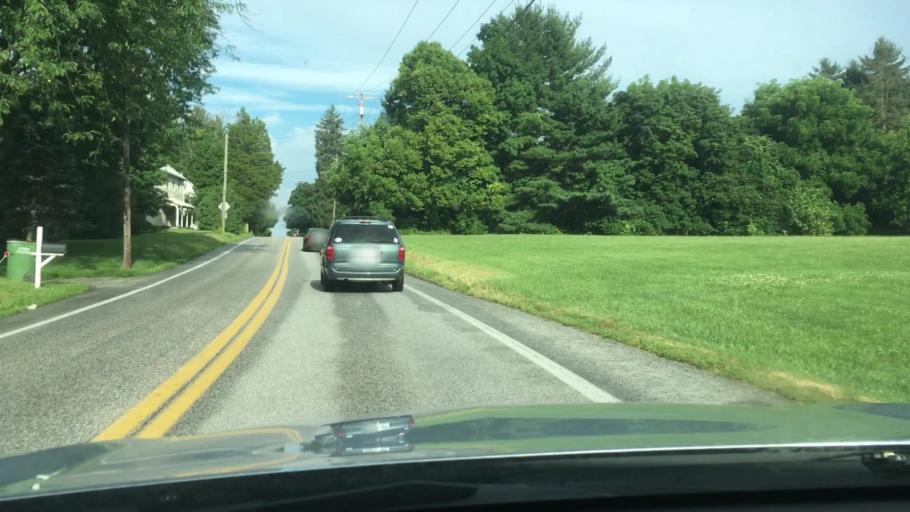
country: US
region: Pennsylvania
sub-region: York County
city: Dillsburg
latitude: 40.1490
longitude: -77.0711
